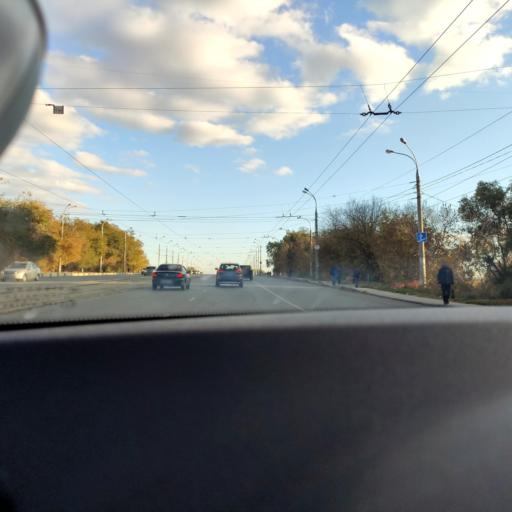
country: RU
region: Samara
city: Samara
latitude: 53.2152
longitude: 50.2679
